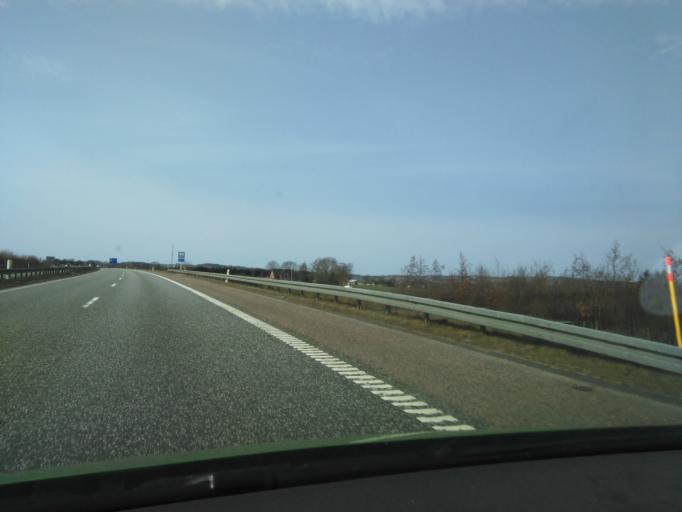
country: DK
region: Central Jutland
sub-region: Skanderborg Kommune
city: Galten
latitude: 56.1477
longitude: 9.8401
